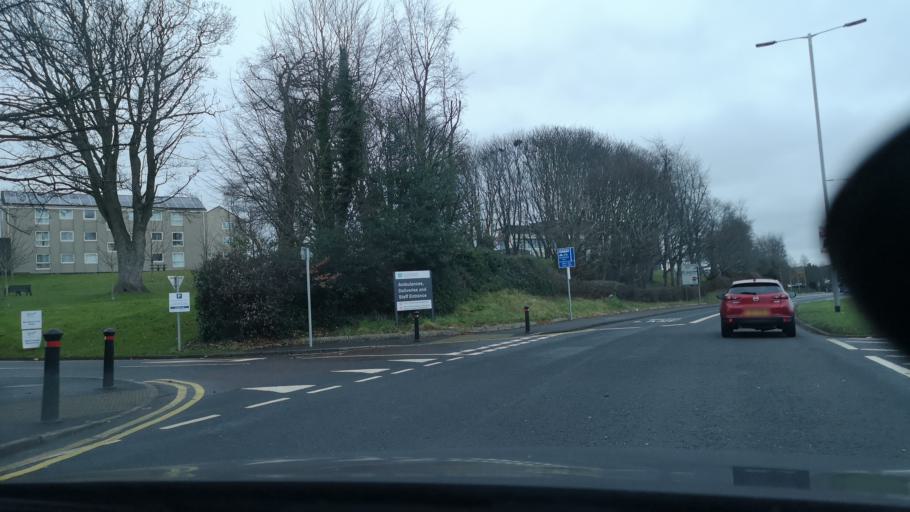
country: GB
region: Northern Ireland
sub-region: Castlereagh District
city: Dundonald
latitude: 54.5949
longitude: -5.8155
